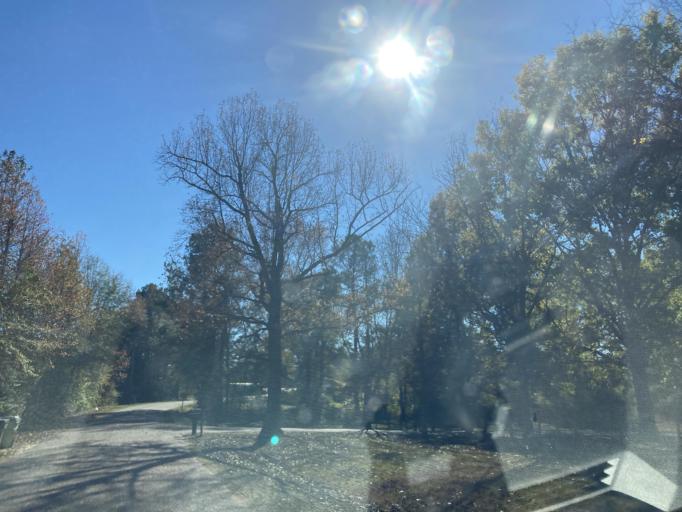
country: US
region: Mississippi
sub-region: Lamar County
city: Sumrall
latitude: 31.3003
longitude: -89.6413
